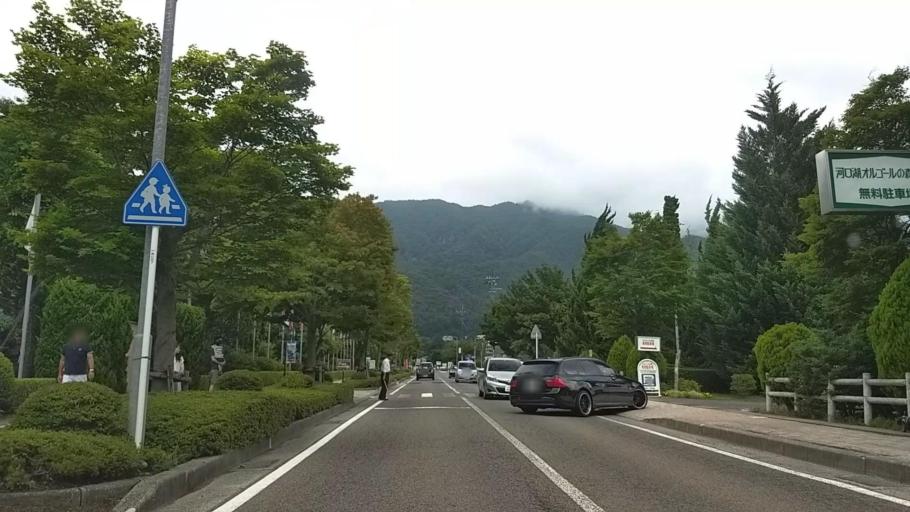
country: JP
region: Yamanashi
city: Fujikawaguchiko
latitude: 35.5222
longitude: 138.7696
